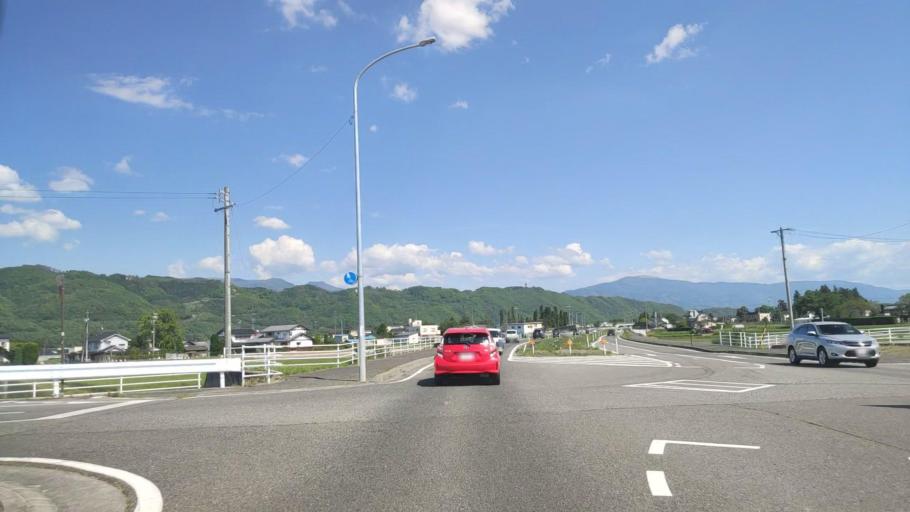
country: JP
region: Nagano
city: Toyoshina
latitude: 36.2788
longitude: 137.9234
